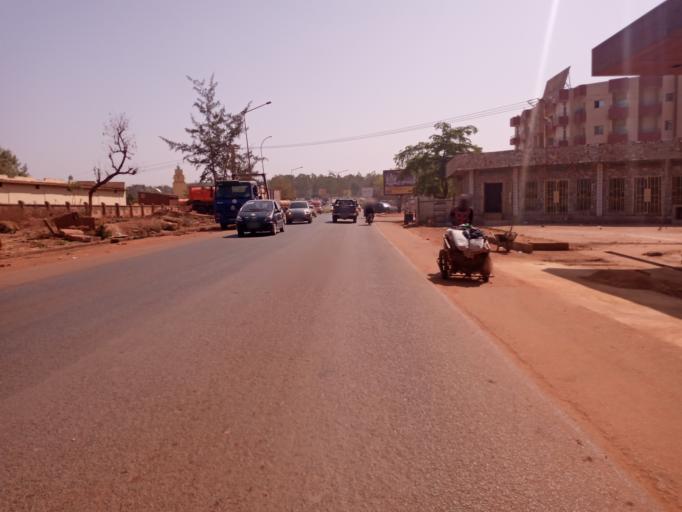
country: ML
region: Bamako
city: Bamako
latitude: 12.6076
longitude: -8.0007
